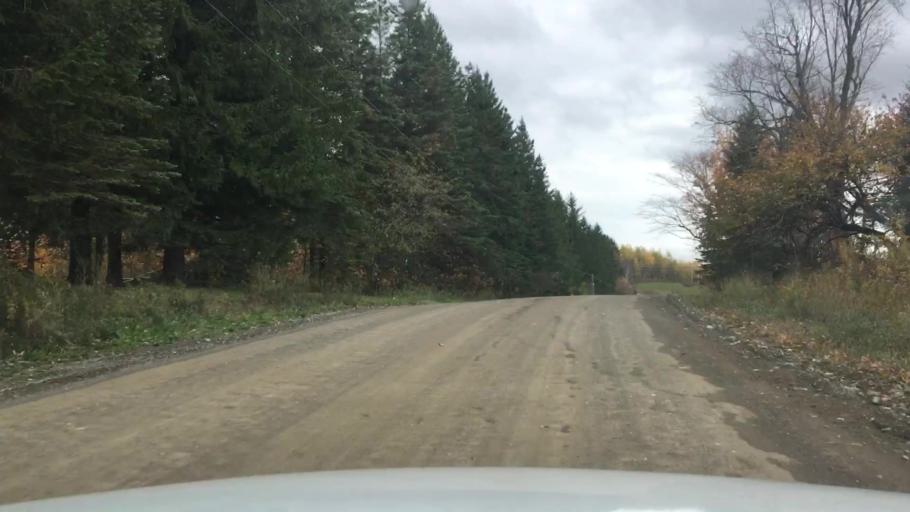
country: US
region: Maine
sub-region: Aroostook County
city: Easton
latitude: 46.5206
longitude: -67.8876
